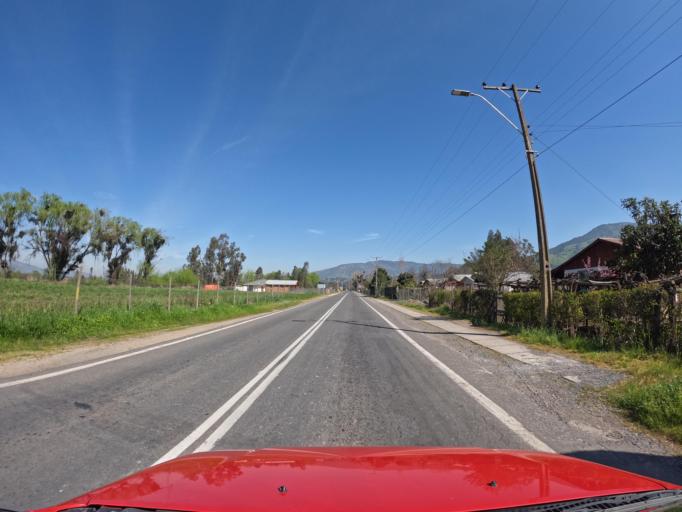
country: CL
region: Maule
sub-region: Provincia de Curico
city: Rauco
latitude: -34.9790
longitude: -71.3987
